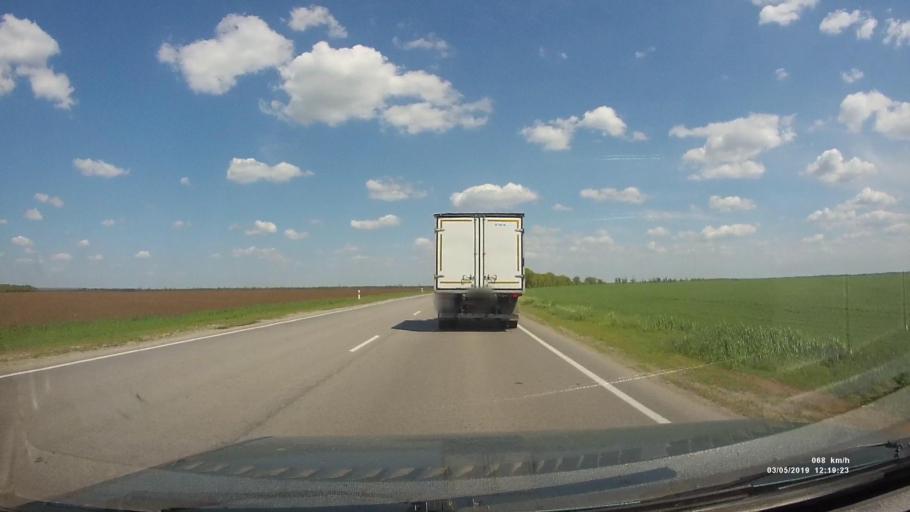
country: RU
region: Rostov
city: Melikhovskaya
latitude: 47.4002
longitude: 40.6075
